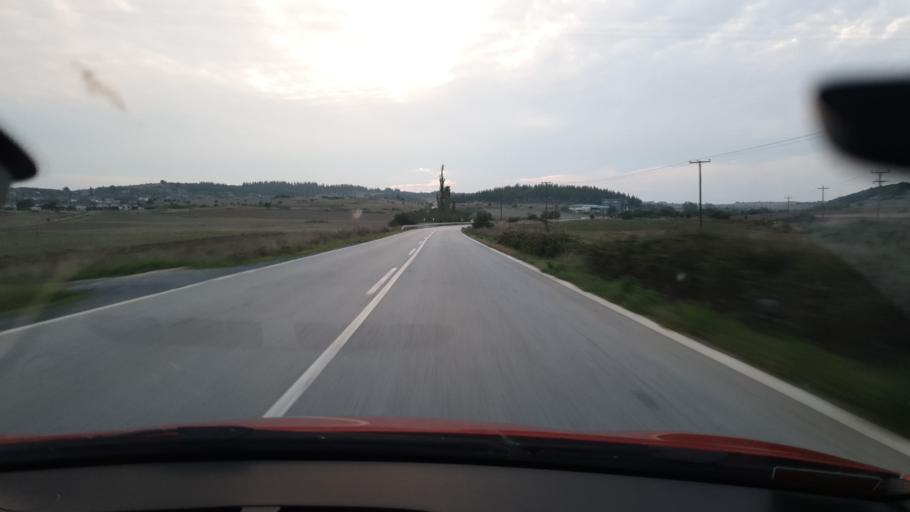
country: GR
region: Central Macedonia
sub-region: Nomos Kilkis
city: Kristoni
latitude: 40.9952
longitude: 22.7445
